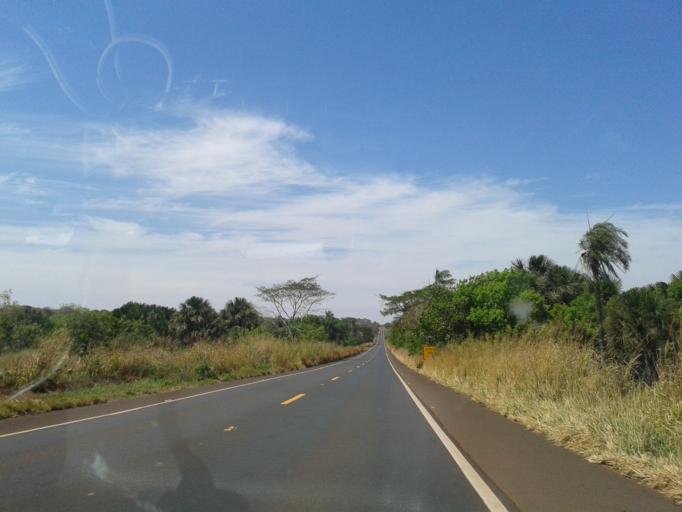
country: BR
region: Minas Gerais
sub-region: Santa Vitoria
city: Santa Vitoria
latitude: -18.8973
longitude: -49.9536
